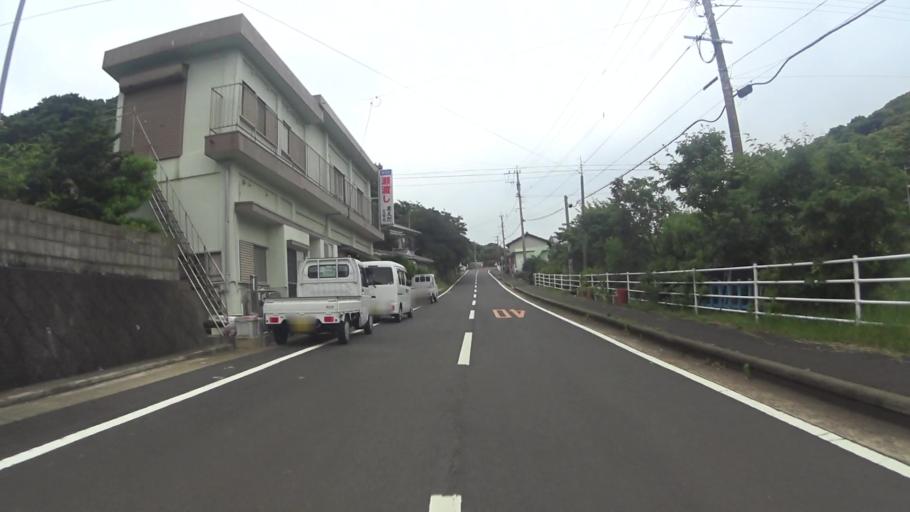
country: JP
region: Nagasaki
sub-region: Hirado Shi
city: Hirado
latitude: 33.1945
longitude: 129.3625
